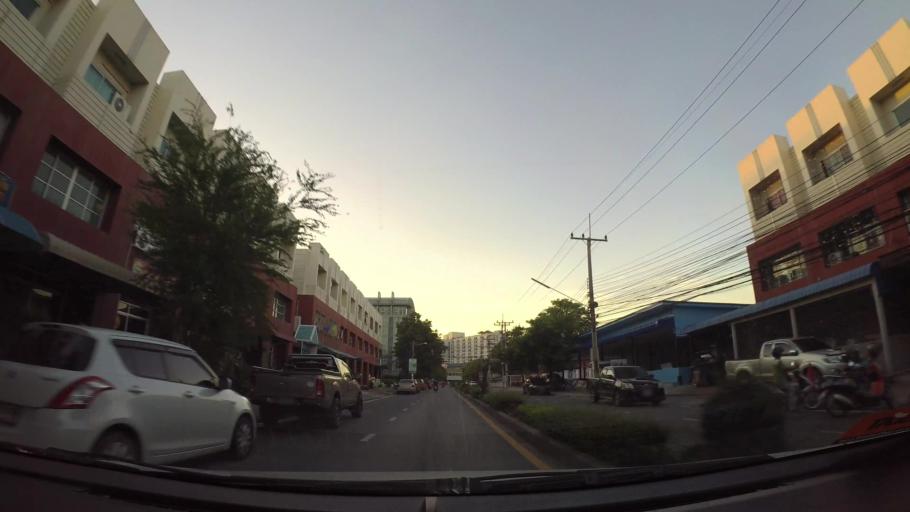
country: TH
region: Chon Buri
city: Bang Lamung
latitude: 13.0918
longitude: 100.9179
